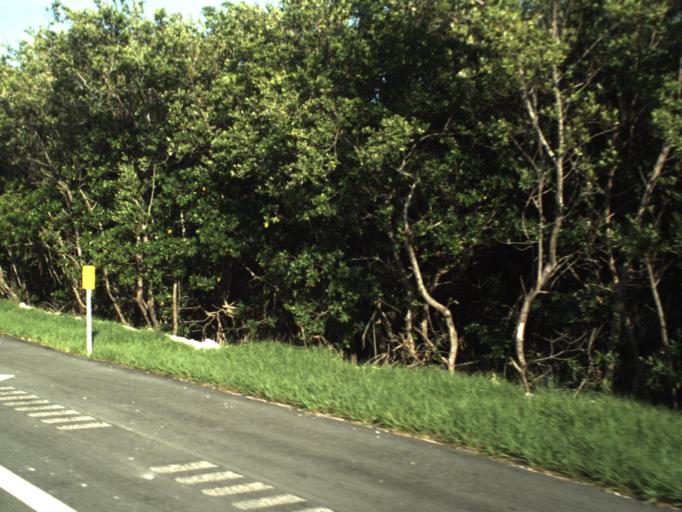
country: US
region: Florida
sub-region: Monroe County
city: Marathon
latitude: 24.7494
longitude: -80.9754
